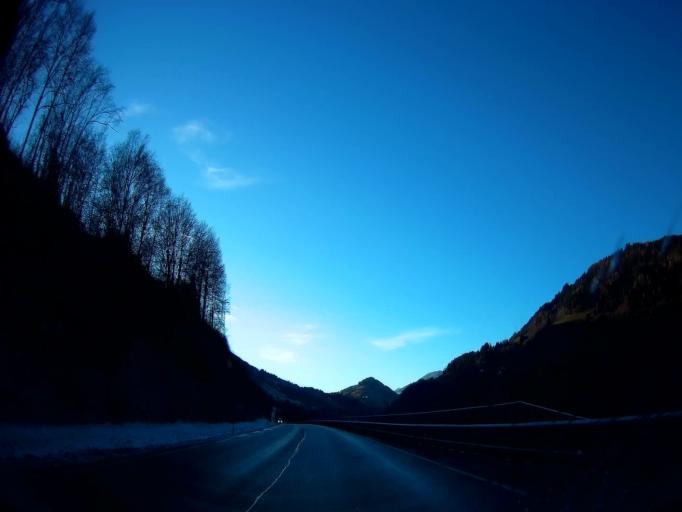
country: AT
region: Salzburg
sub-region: Politischer Bezirk Zell am See
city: Lend
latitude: 47.2979
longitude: 13.0785
